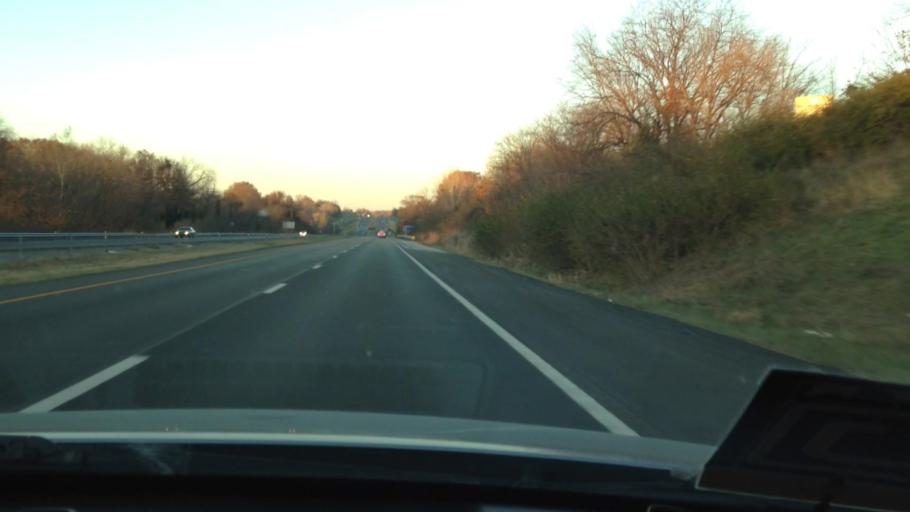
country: US
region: Missouri
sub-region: Clay County
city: Gladstone
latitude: 39.2082
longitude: -94.5895
